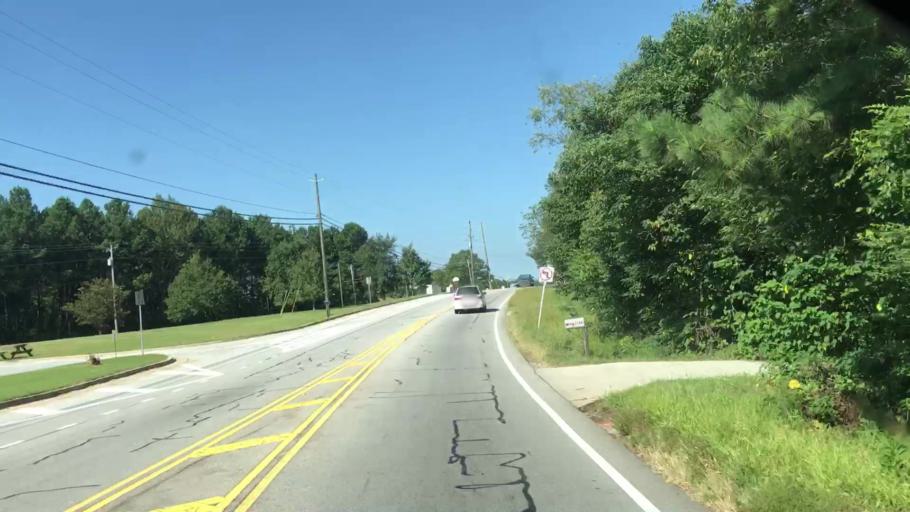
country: US
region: Georgia
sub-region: Walton County
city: Loganville
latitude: 33.8543
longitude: -83.8752
